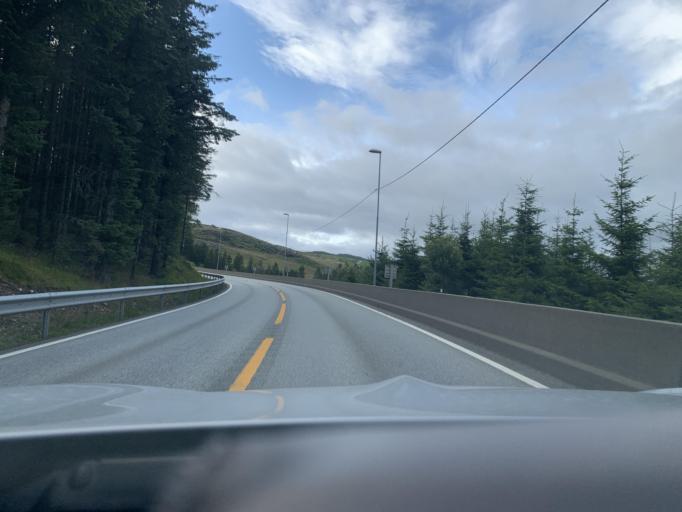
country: NO
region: Rogaland
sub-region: Bjerkreim
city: Vikesa
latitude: 58.6392
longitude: 6.0830
